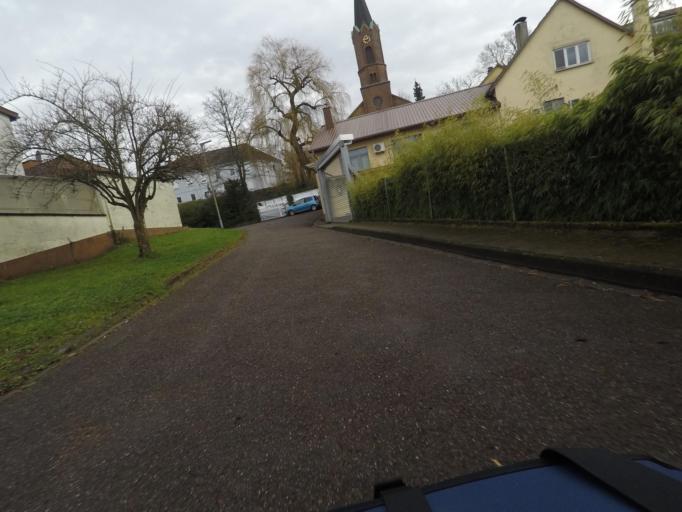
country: DE
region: Baden-Wuerttemberg
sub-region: Karlsruhe Region
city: Rheinstetten
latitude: 48.9752
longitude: 8.3060
